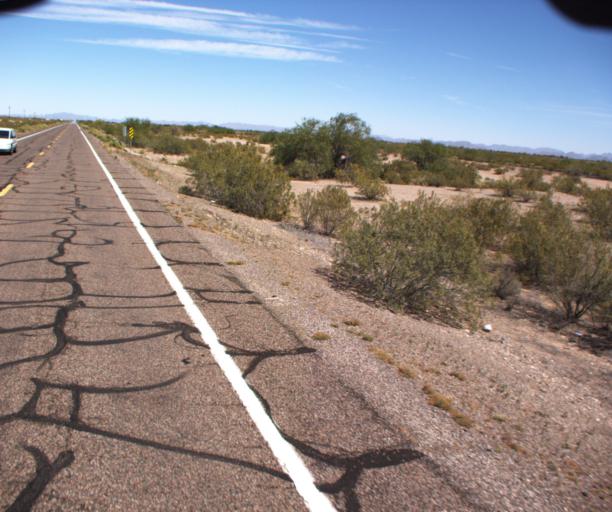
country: US
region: Arizona
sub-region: Maricopa County
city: Gila Bend
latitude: 32.8103
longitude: -112.7938
